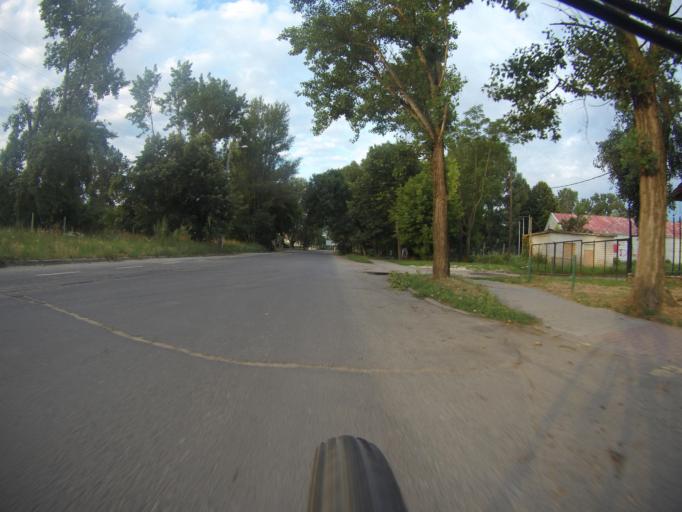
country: HU
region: Budapest
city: Budapest XIII. keruelet
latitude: 47.5434
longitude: 19.0677
